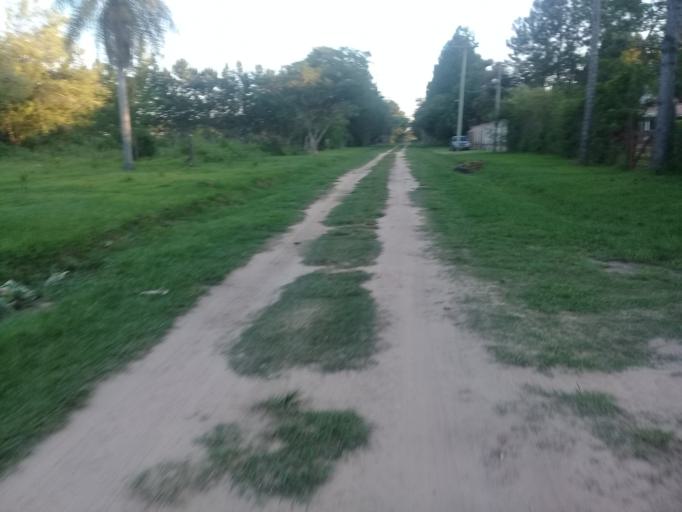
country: AR
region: Corrientes
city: San Luis del Palmar
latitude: -27.4684
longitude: -58.6669
